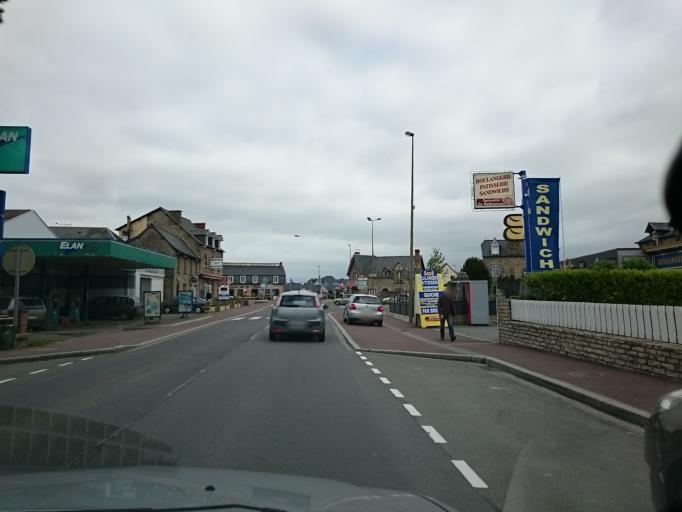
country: FR
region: Lower Normandy
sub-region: Departement de la Manche
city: Pontorson
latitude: 48.5972
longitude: -1.5128
